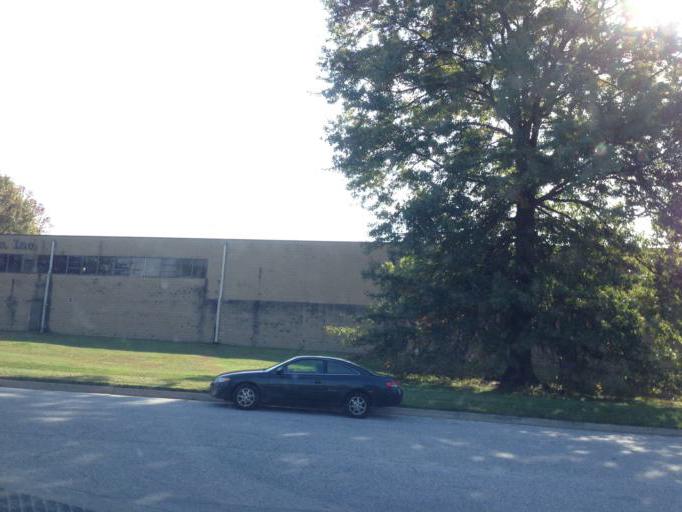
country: US
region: Maryland
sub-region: Howard County
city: Ellicott City
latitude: 39.2773
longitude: -76.8147
